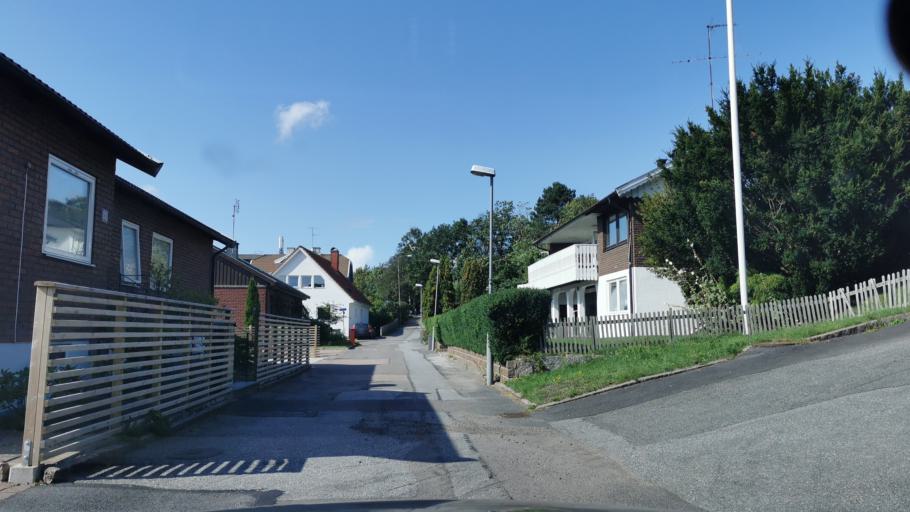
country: SE
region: Vaestra Goetaland
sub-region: Goteborg
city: Majorna
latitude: 57.6388
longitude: 11.9076
